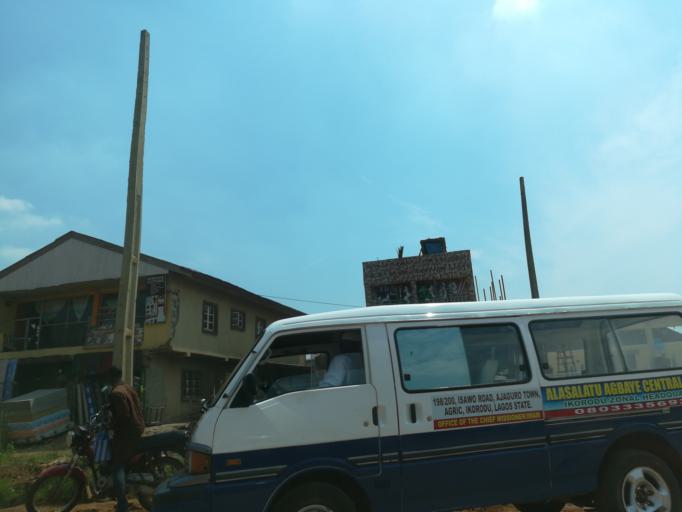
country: NG
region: Lagos
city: Ikorodu
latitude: 6.6469
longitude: 3.4788
